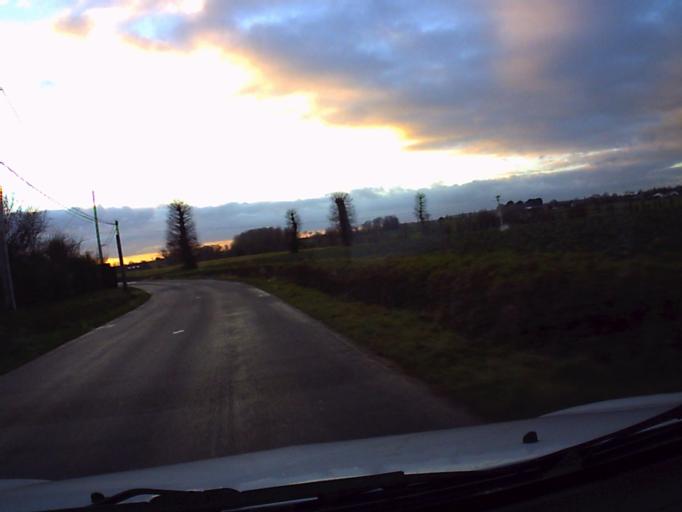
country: FR
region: Brittany
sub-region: Departement d'Ille-et-Vilaine
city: Bedee
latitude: 48.1784
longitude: -1.9590
